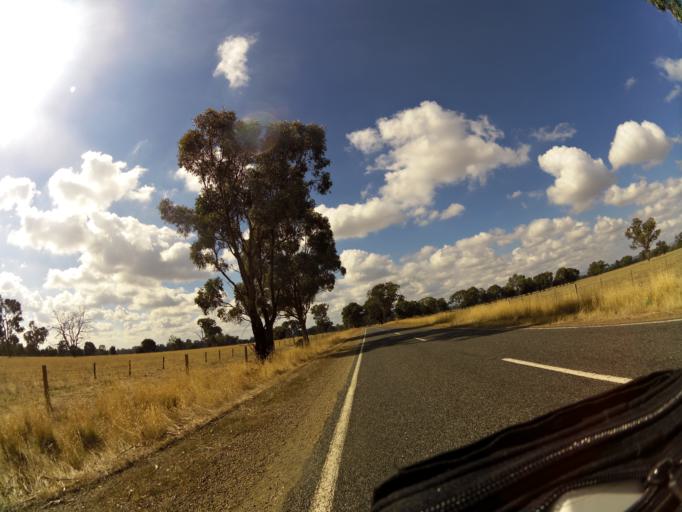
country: AU
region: Victoria
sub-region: Benalla
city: Benalla
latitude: -36.6081
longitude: 146.0166
